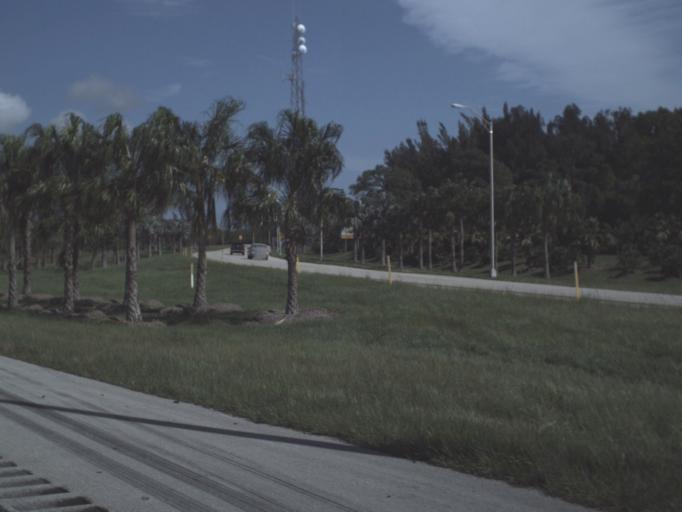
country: US
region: Florida
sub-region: Saint Lucie County
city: Fort Pierce South
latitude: 27.4059
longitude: -80.3992
